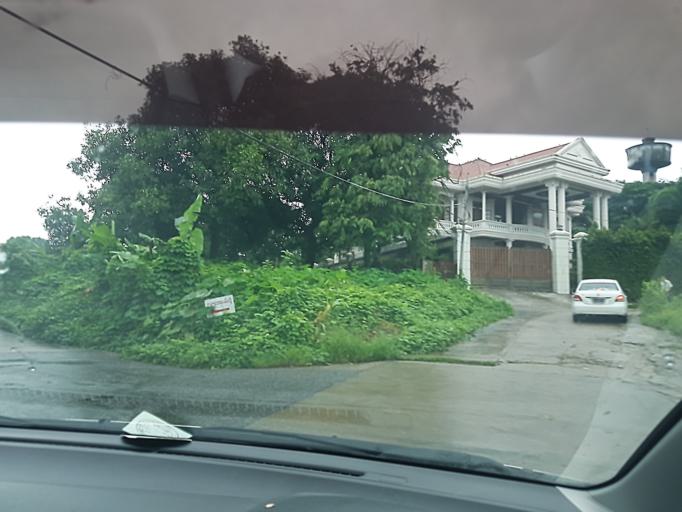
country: MM
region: Yangon
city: Yangon
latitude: 16.8124
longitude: 96.1517
